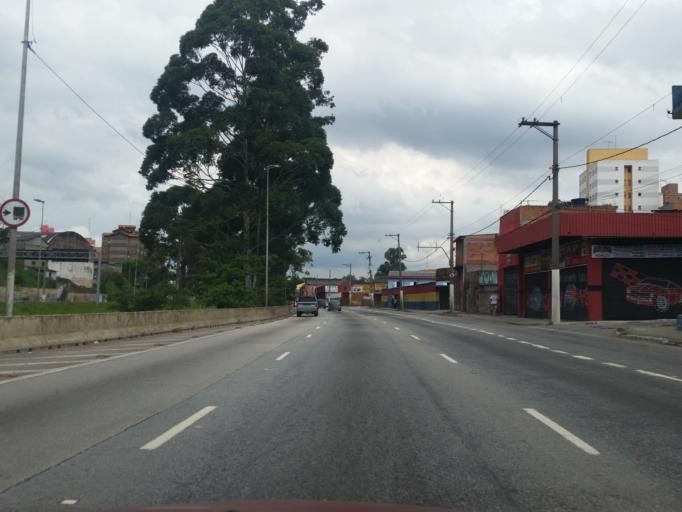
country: BR
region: Sao Paulo
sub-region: Ferraz De Vasconcelos
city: Ferraz de Vasconcelos
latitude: -23.5523
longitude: -46.4465
